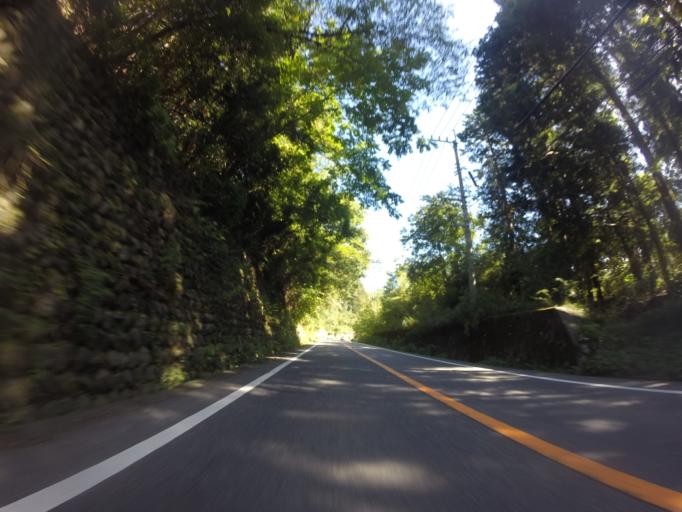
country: JP
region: Shizuoka
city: Fujinomiya
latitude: 35.3471
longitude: 138.4506
